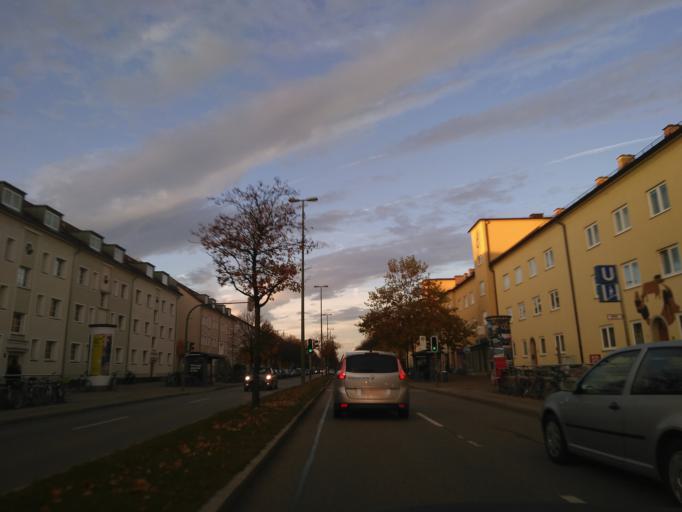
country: DE
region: Bavaria
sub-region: Upper Bavaria
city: Munich
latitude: 48.0967
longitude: 11.5781
